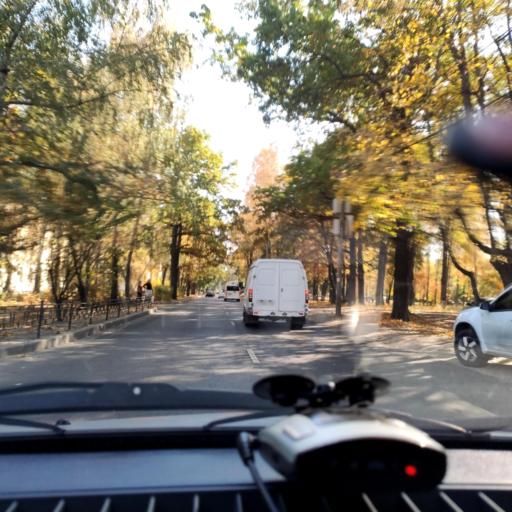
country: RU
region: Voronezj
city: Voronezh
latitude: 51.7212
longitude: 39.2186
